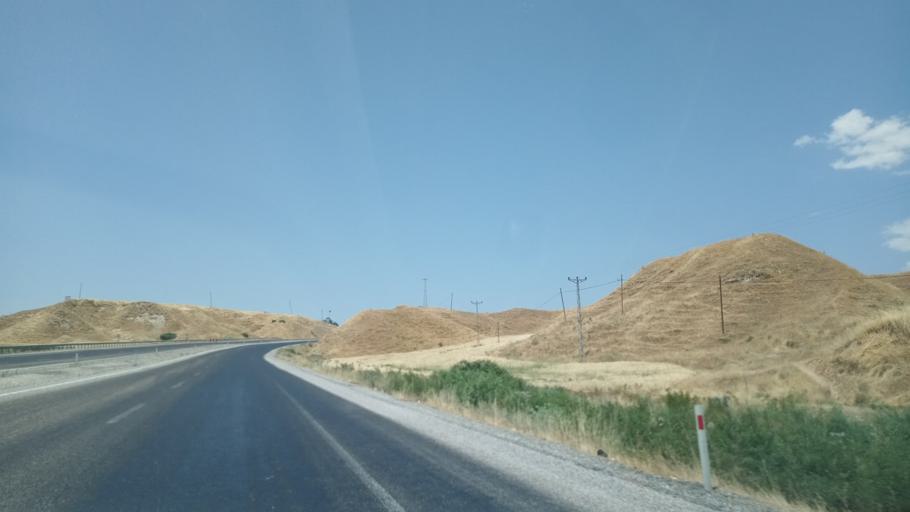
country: TR
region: Batman
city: Bekirhan
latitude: 38.1546
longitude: 41.3797
